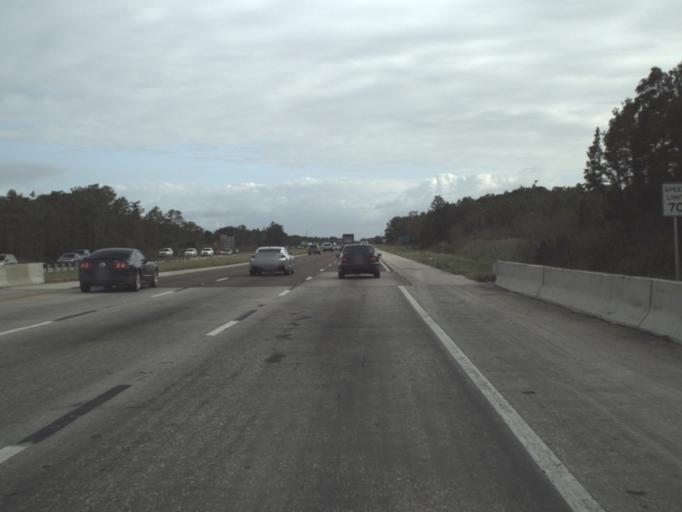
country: US
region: Florida
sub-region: Lee County
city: Fort Myers
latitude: 26.6031
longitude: -81.8006
